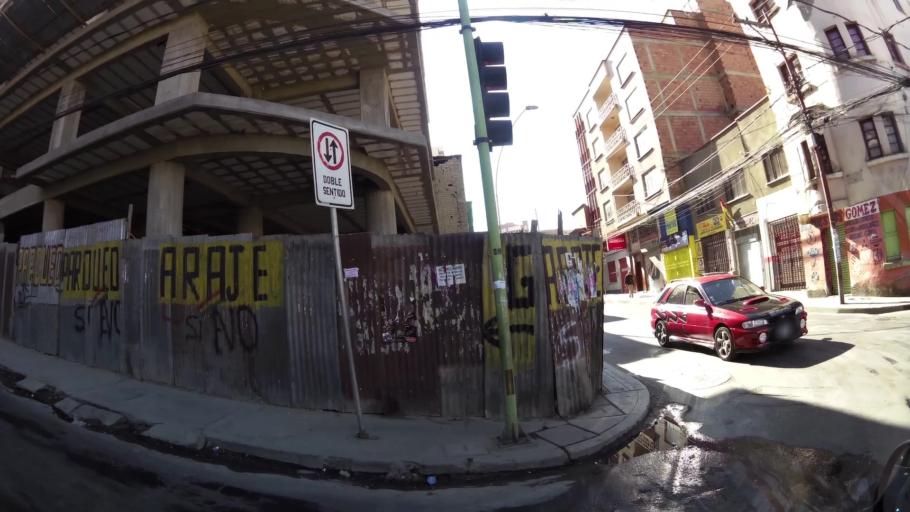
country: BO
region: La Paz
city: La Paz
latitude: -16.5044
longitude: -68.1353
